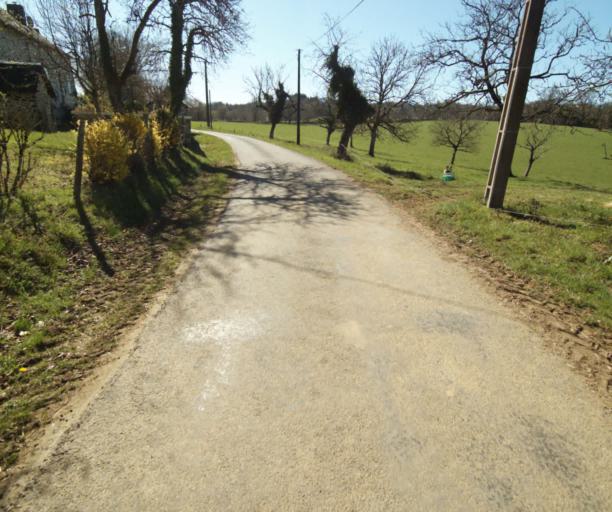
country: FR
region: Limousin
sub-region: Departement de la Correze
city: Chamboulive
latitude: 45.4071
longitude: 1.7299
